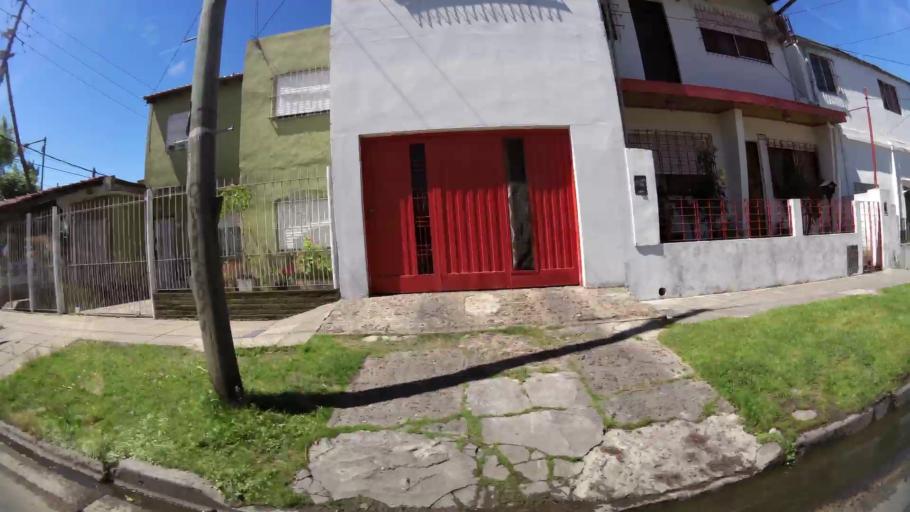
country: AR
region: Buenos Aires
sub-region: Partido de Tigre
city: Tigre
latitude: -34.4983
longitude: -58.5844
